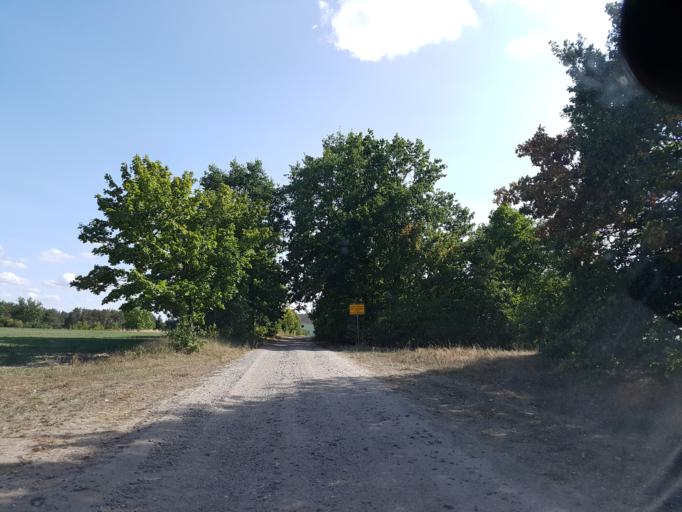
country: DE
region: Brandenburg
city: Treuenbrietzen
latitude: 52.0275
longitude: 12.8132
